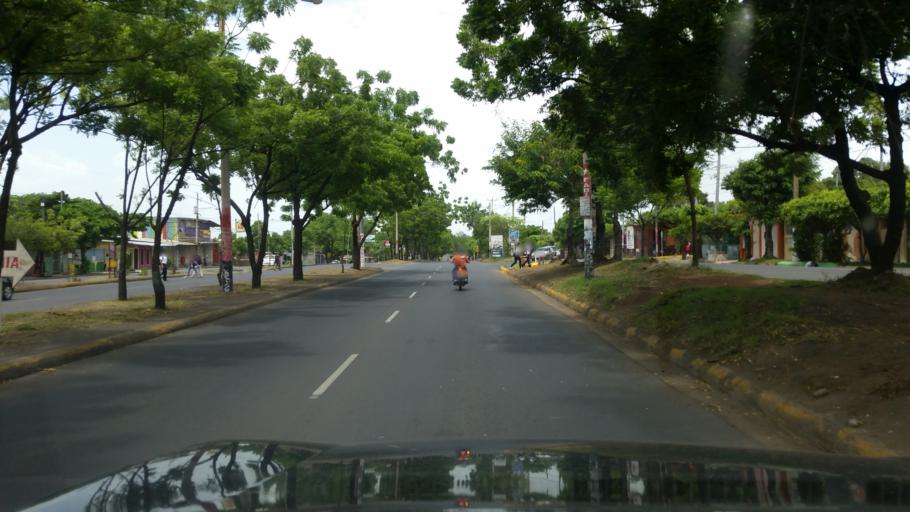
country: NI
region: Managua
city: Managua
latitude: 12.1401
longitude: -86.2136
